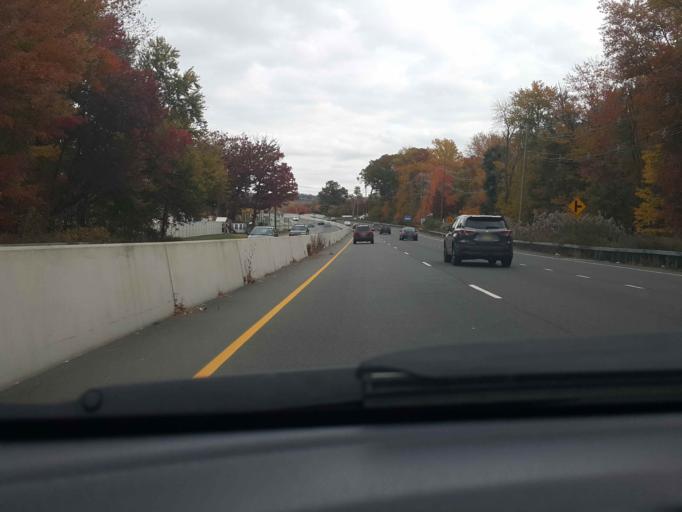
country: US
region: New York
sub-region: Rockland County
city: West Nyack
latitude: 41.0924
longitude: -73.9692
